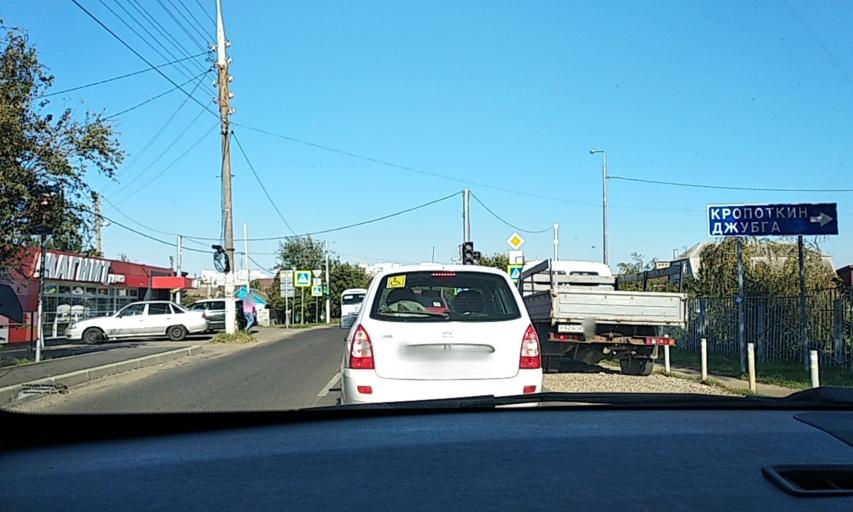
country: RU
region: Krasnodarskiy
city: Pashkovskiy
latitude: 45.0319
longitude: 39.1207
